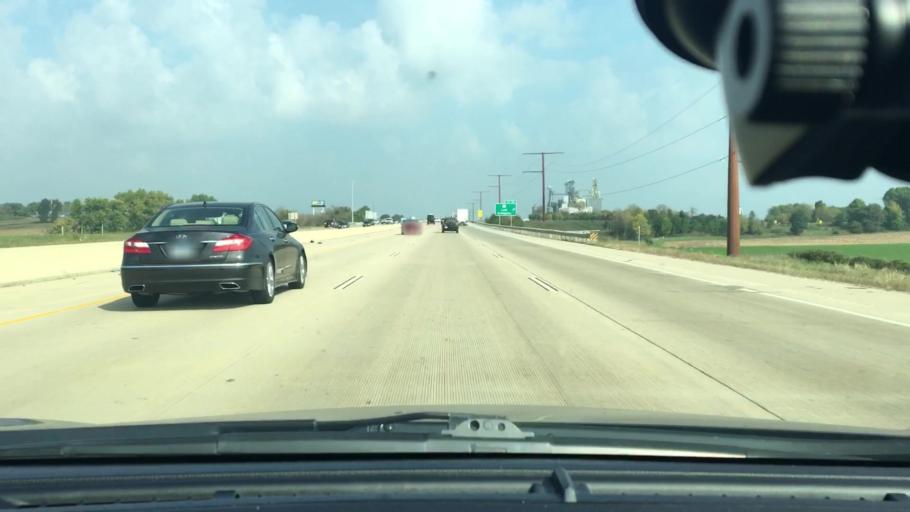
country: US
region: Wisconsin
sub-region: Columbia County
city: Lodi
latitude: 43.3323
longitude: -89.4525
